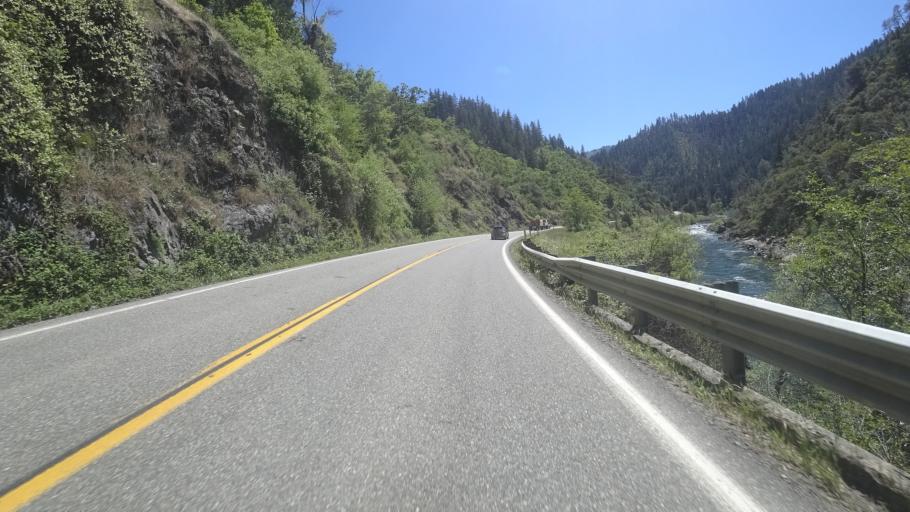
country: US
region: California
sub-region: Trinity County
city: Hayfork
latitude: 40.7607
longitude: -123.2817
